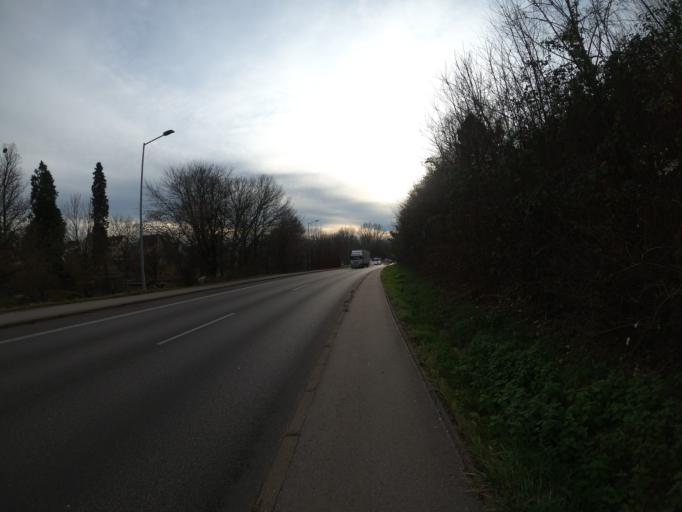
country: DE
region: Baden-Wuerttemberg
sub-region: Regierungsbezirk Stuttgart
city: Goeppingen
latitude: 48.7152
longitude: 9.6485
